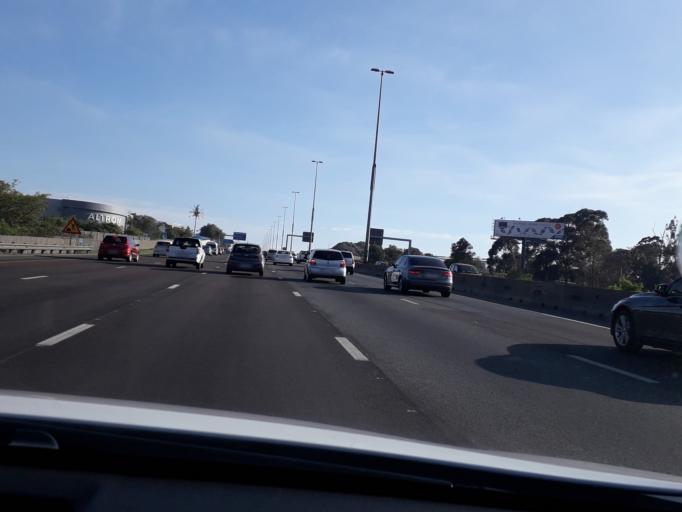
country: ZA
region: Gauteng
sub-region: City of Johannesburg Metropolitan Municipality
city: Midrand
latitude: -25.9894
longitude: 28.1233
